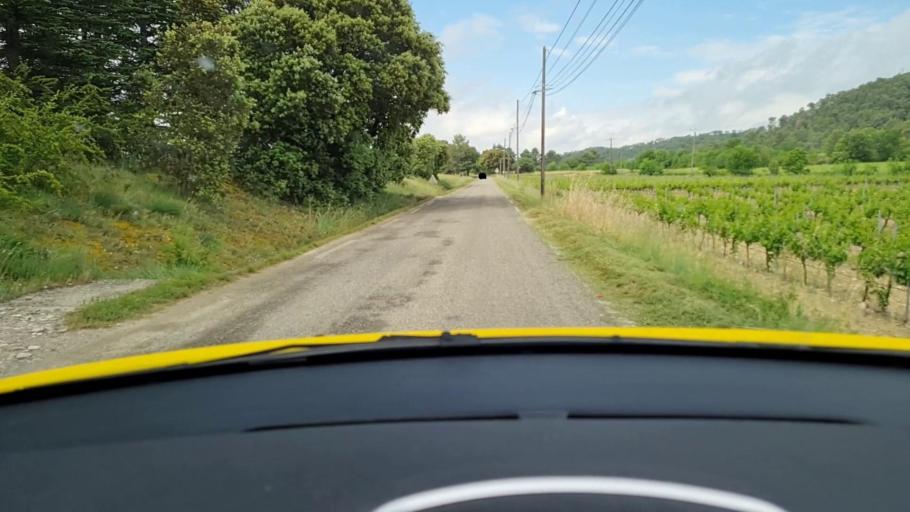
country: FR
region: Languedoc-Roussillon
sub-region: Departement du Gard
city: Quissac
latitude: 43.8542
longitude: 4.0115
